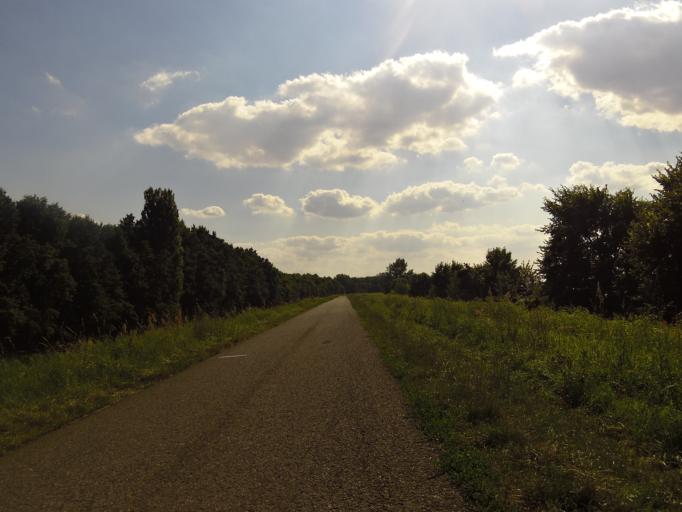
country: HU
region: Jasz-Nagykun-Szolnok
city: Tiszaszolos
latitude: 47.5418
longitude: 20.6487
